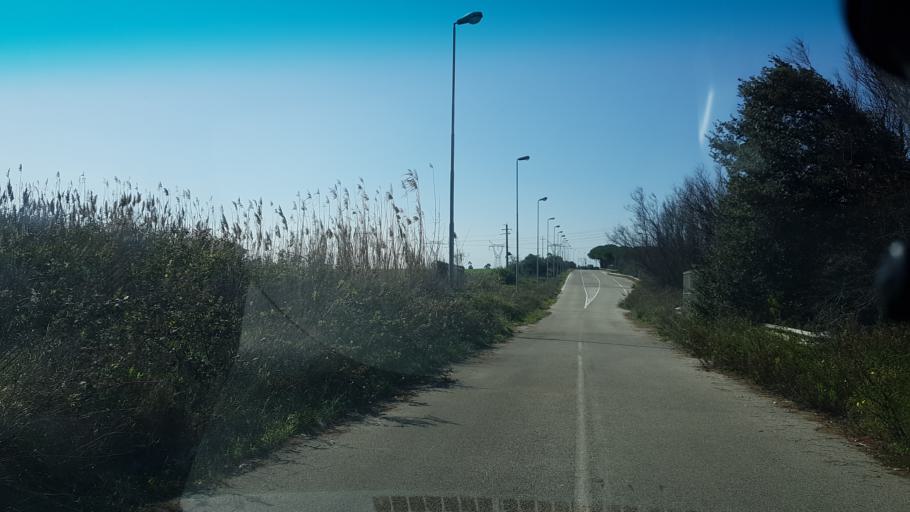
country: IT
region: Apulia
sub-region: Provincia di Brindisi
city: Torchiarolo
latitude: 40.5598
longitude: 18.0399
